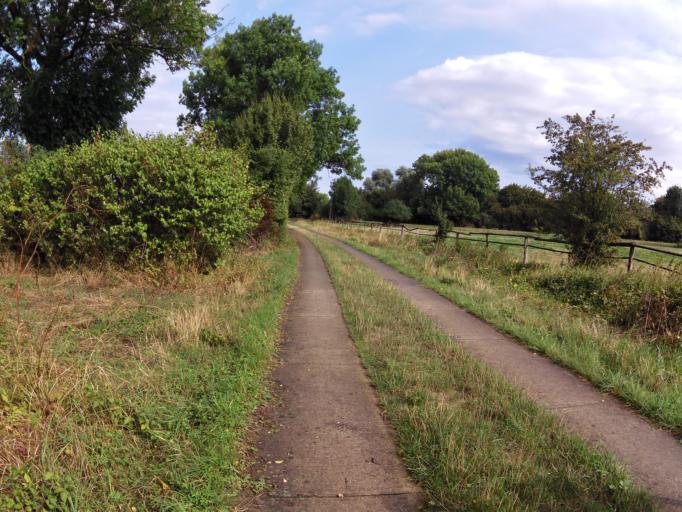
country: DE
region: Lower Saxony
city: Marklohe
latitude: 52.6615
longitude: 9.1801
